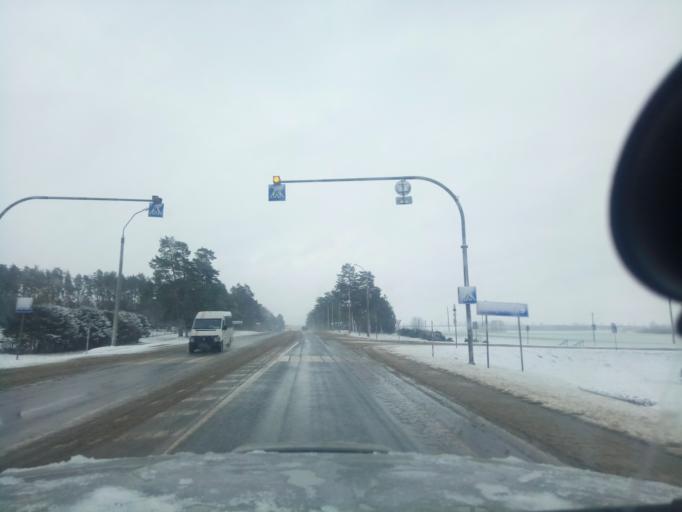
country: BY
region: Minsk
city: Nyasvizh
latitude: 53.2469
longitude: 26.6248
